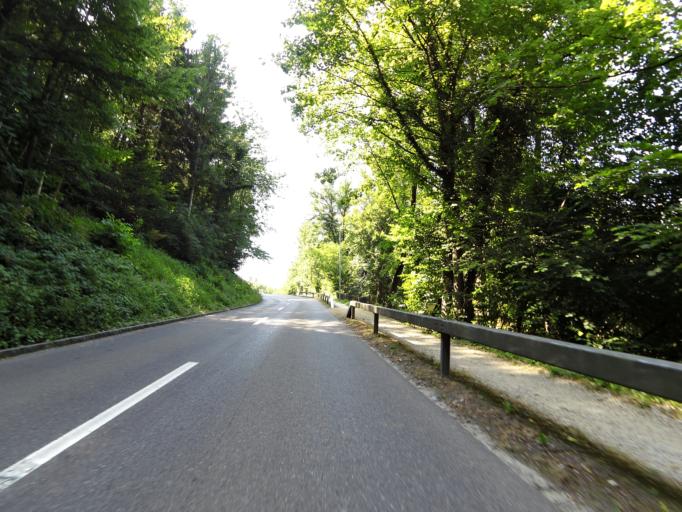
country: CH
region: Aargau
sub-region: Bezirk Baden
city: Birmenstorf
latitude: 47.4584
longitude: 8.2439
